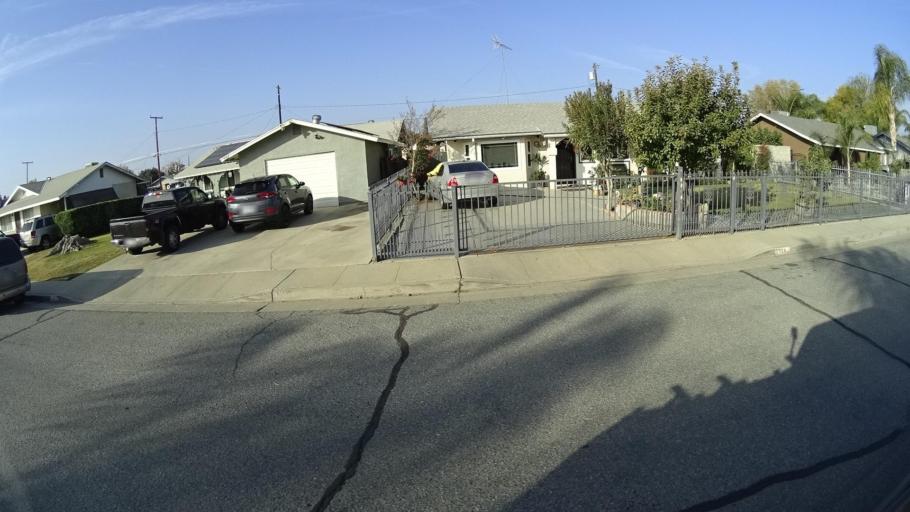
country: US
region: California
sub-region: Kern County
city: McFarland
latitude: 35.6785
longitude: -119.2185
